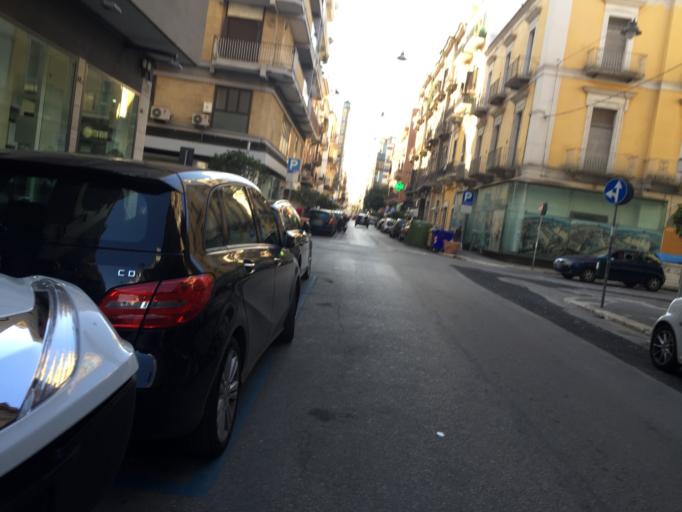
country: IT
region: Apulia
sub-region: Provincia di Bari
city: Bari
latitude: 41.1244
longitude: 16.8610
